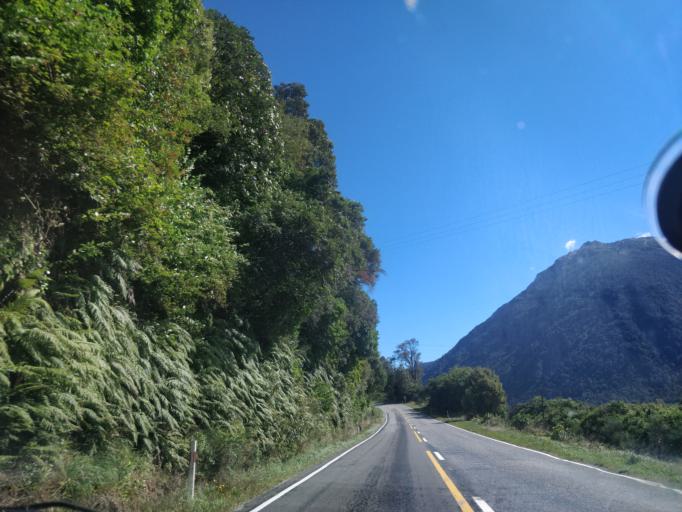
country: NZ
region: West Coast
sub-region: Grey District
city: Greymouth
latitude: -42.7618
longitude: 171.5775
